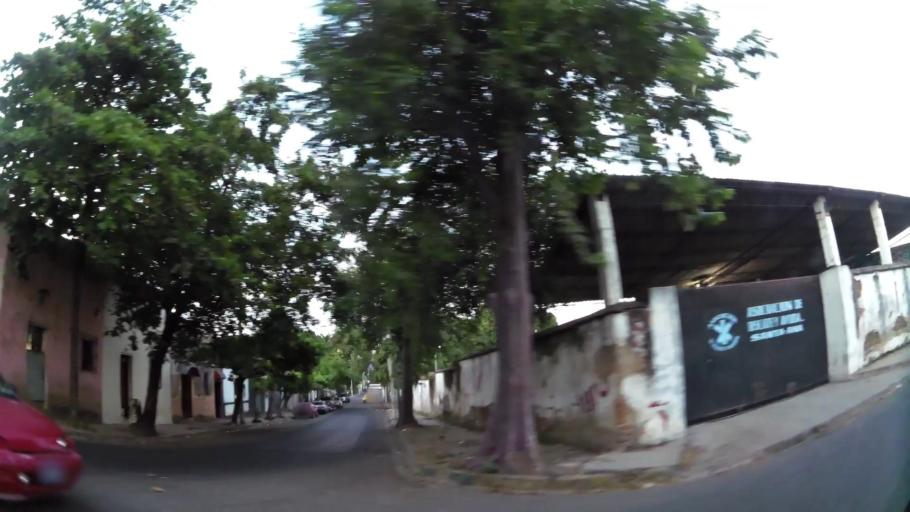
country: SV
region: Santa Ana
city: Santa Ana
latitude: 13.9884
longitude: -89.5535
